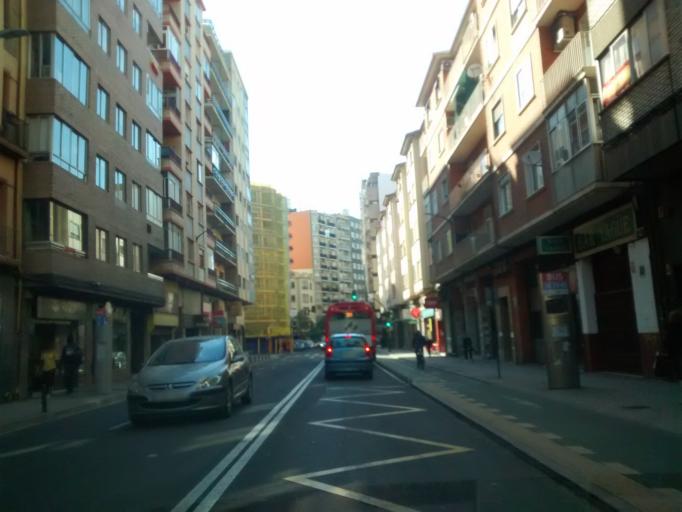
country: ES
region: Aragon
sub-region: Provincia de Zaragoza
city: Zaragoza
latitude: 41.6475
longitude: -0.8740
